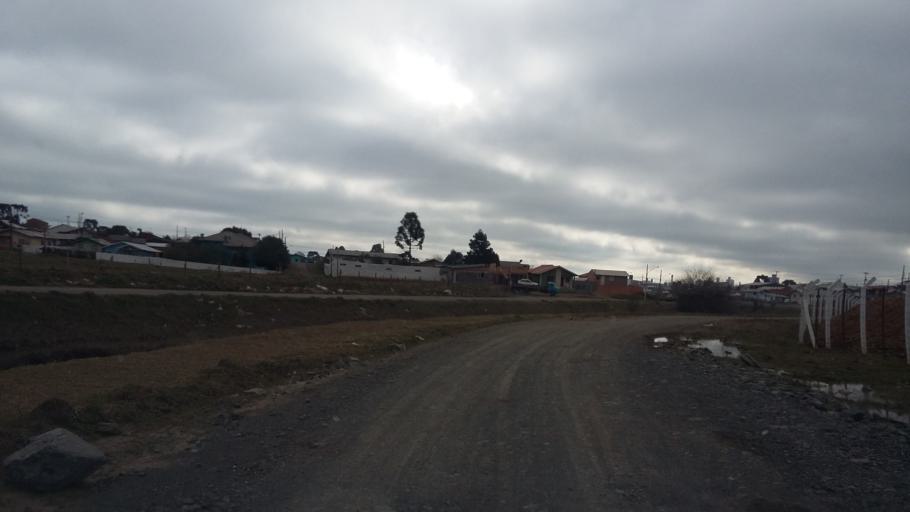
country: BR
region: Santa Catarina
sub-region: Lages
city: Lages
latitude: -27.8365
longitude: -50.3220
